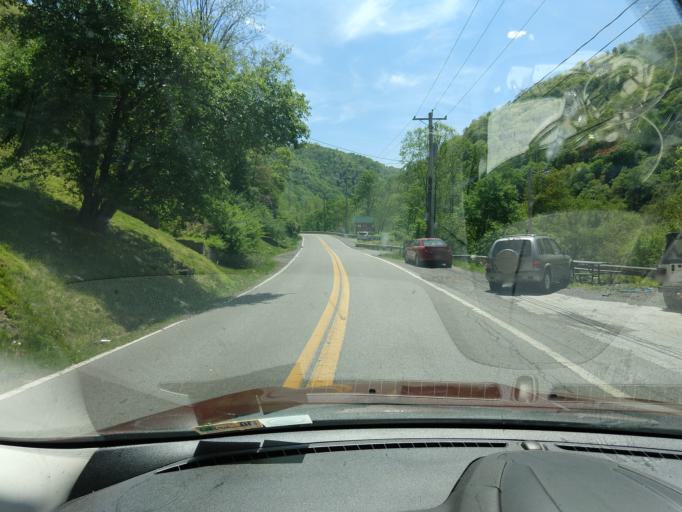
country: US
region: West Virginia
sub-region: McDowell County
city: Welch
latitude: 37.3066
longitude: -81.6929
